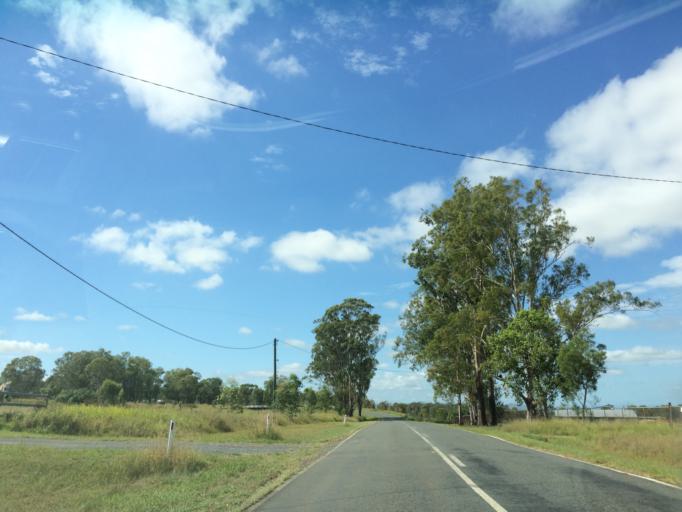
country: AU
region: Queensland
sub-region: Logan
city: Cedar Vale
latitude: -27.8864
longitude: 152.9725
